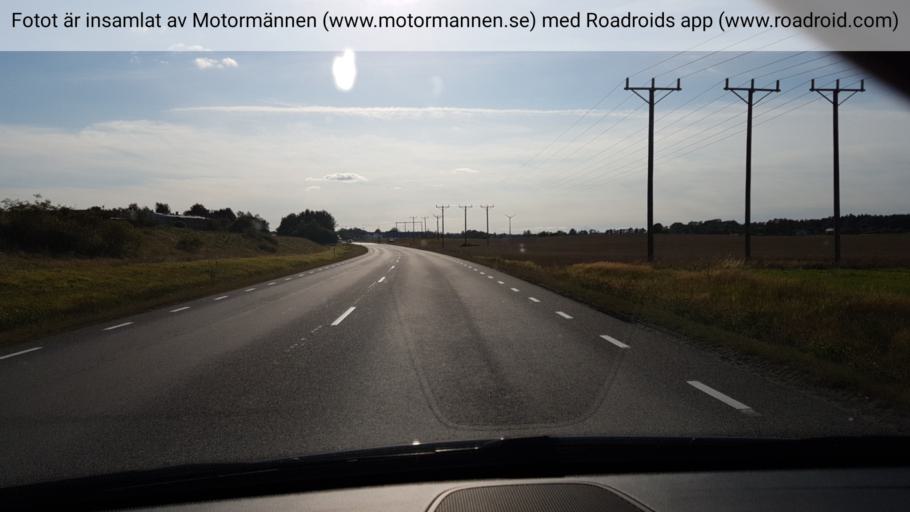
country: SE
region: Vaestra Goetaland
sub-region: Skara Kommun
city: Skara
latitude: 58.3939
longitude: 13.4484
